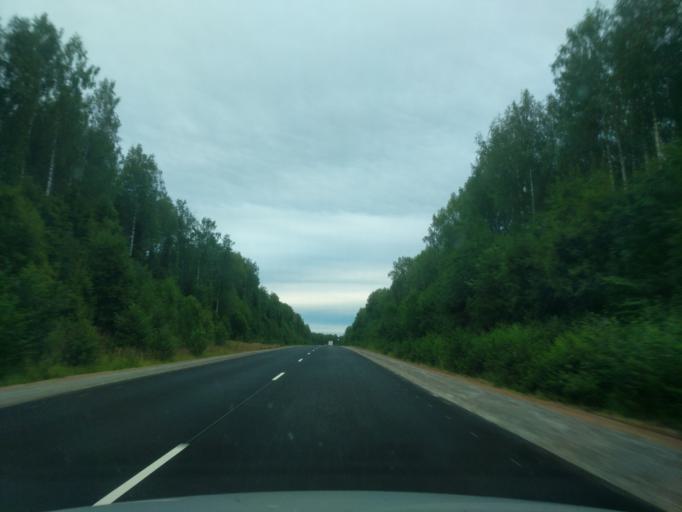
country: RU
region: Kostroma
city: Ponazyrevo
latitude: 58.3259
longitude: 46.6124
